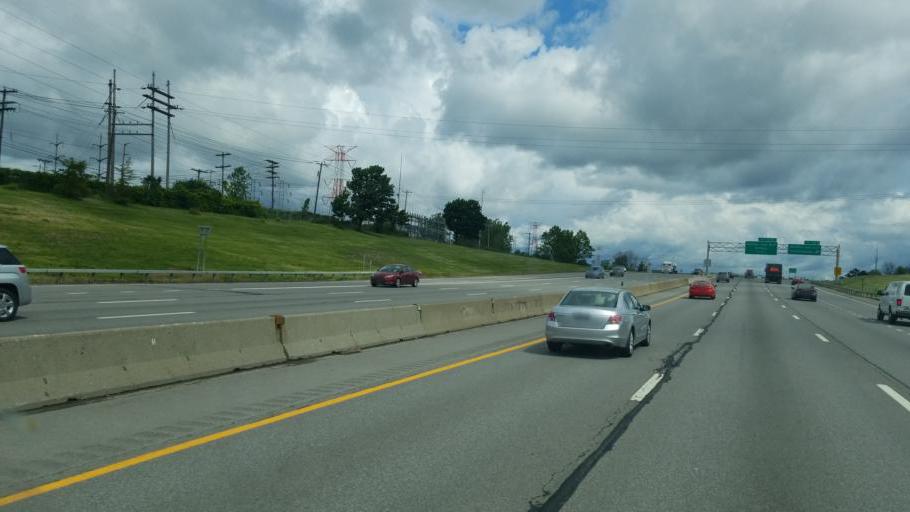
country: US
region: New York
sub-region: Erie County
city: Cheektowaga
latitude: 42.9031
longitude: -78.7669
